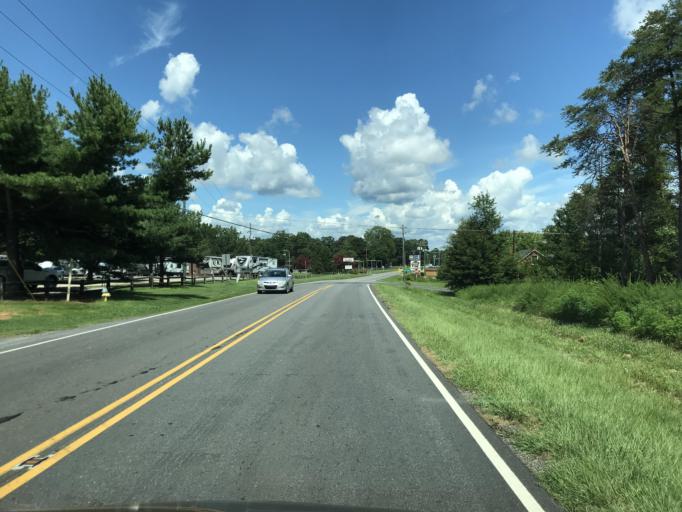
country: US
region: North Carolina
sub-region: Catawba County
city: Lake Norman of Catawba
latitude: 35.5717
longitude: -81.0431
